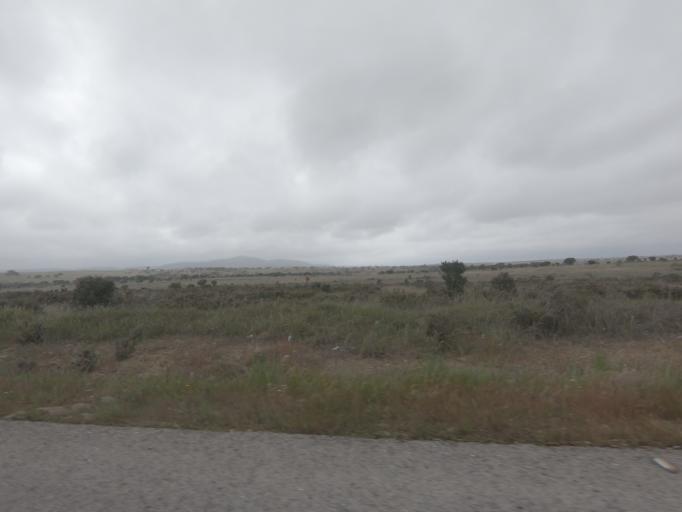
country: ES
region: Extremadura
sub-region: Provincia de Caceres
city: Malpartida de Caceres
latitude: 39.3364
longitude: -6.4816
